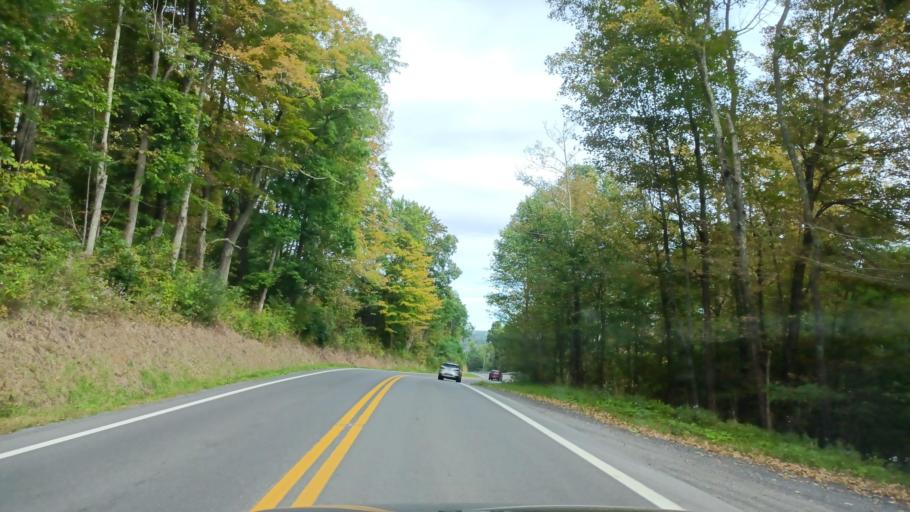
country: US
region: Maryland
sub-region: Garrett County
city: Mountain Lake Park
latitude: 39.2910
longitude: -79.3276
